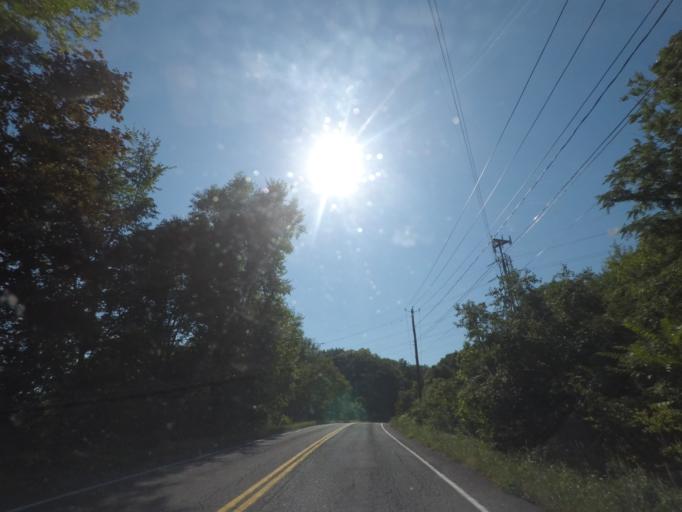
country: US
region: New York
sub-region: Albany County
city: Menands
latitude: 42.7144
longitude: -73.7240
